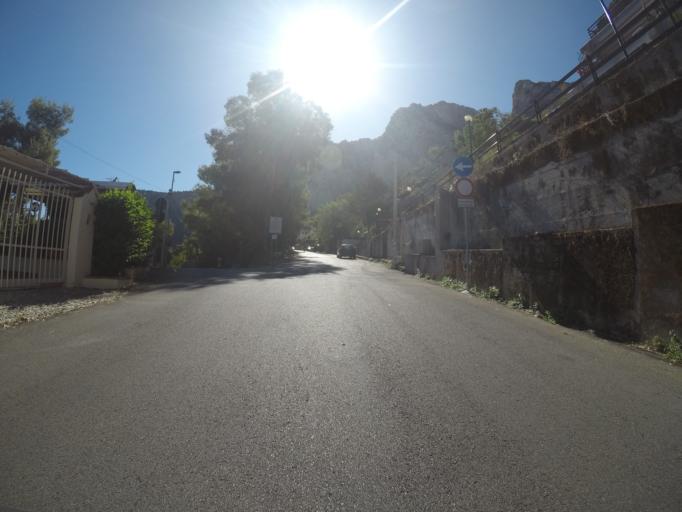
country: IT
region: Sicily
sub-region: Palermo
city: Palermo
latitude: 38.1889
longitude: 13.3407
